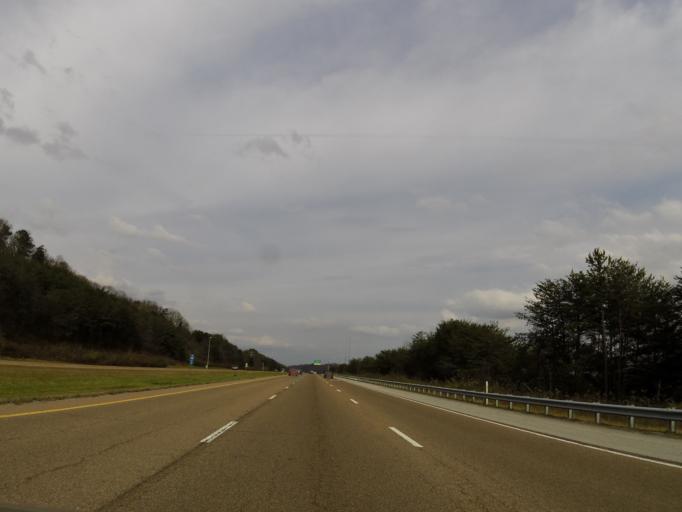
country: US
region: Tennessee
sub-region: Hamilton County
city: Red Bank
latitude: 35.1105
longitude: -85.3082
